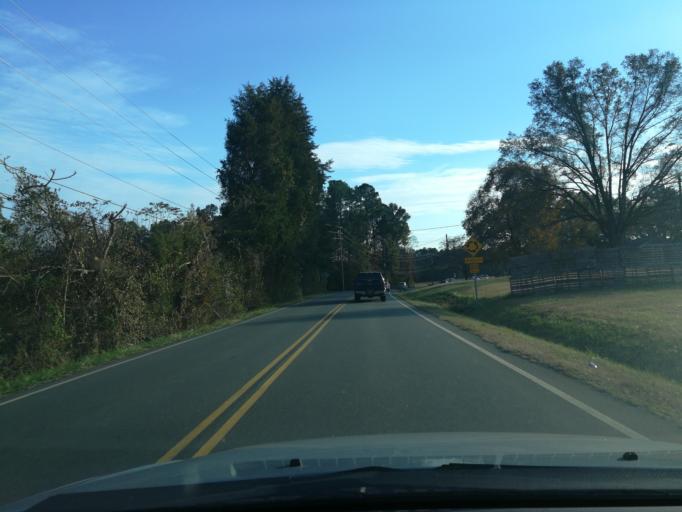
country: US
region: North Carolina
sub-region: Orange County
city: Chapel Hill
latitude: 35.9708
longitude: -79.0076
